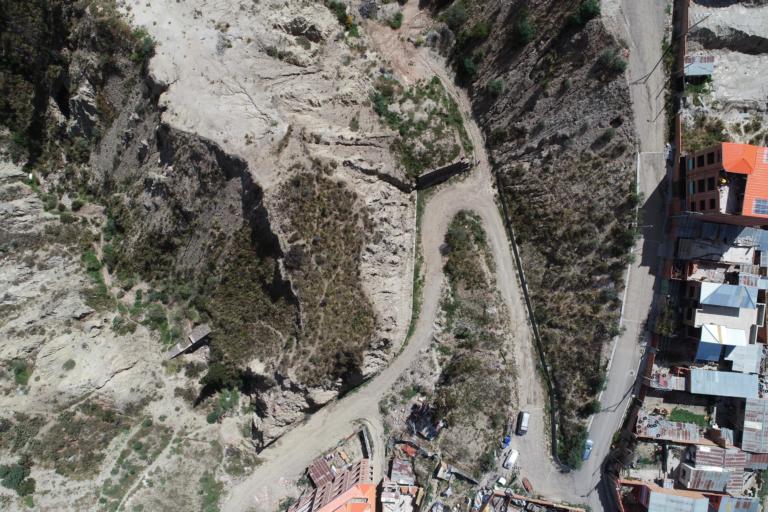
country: BO
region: La Paz
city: La Paz
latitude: -16.5176
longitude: -68.1047
